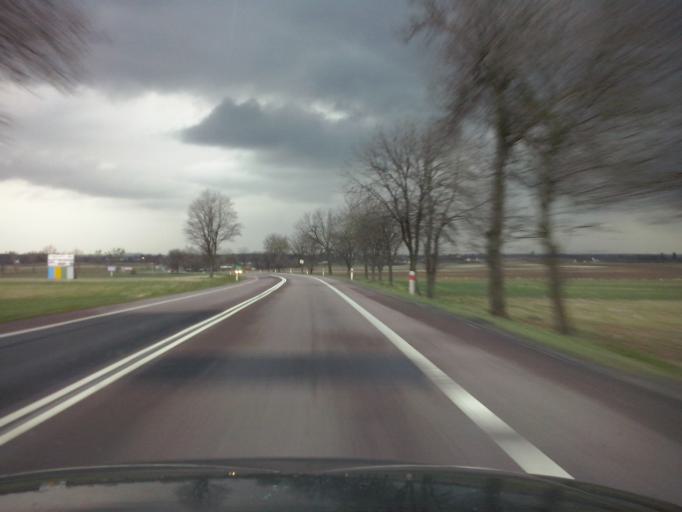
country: PL
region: Lublin Voivodeship
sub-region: Powiat chelmski
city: Rejowiec Fabryczny
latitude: 51.1785
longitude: 23.2105
